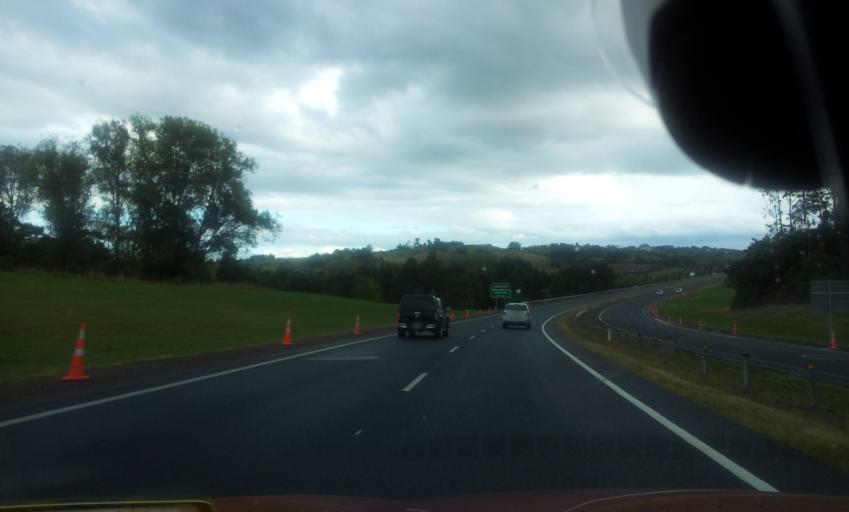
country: NZ
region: Auckland
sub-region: Auckland
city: Rothesay Bay
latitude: -36.6152
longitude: 174.6620
